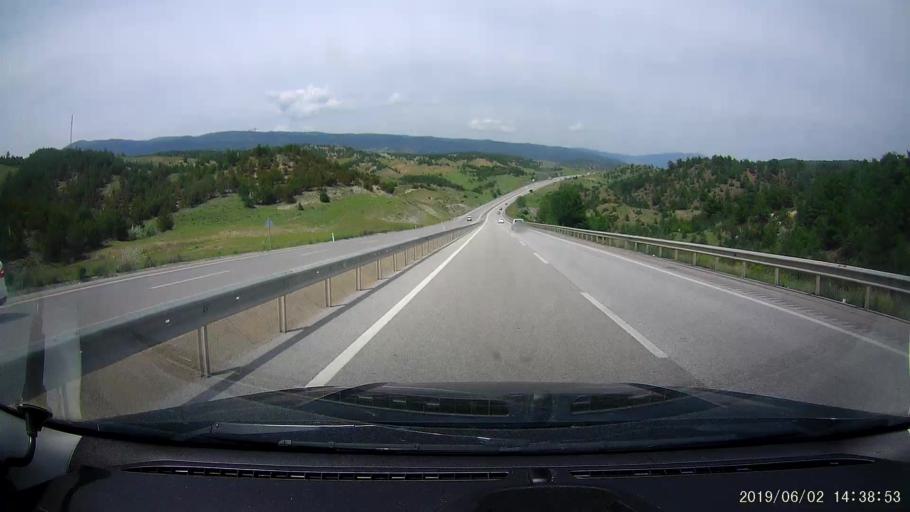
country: TR
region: Corum
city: Hacihamza
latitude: 41.0619
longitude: 34.2897
